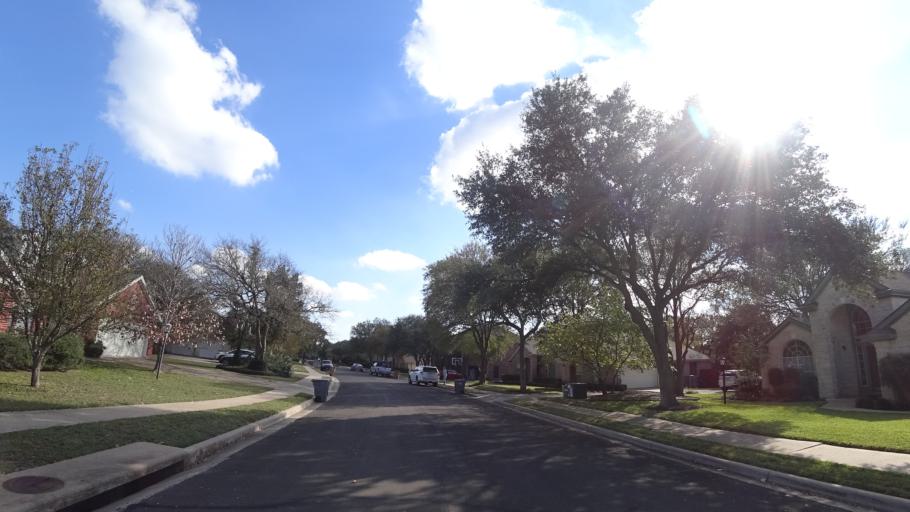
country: US
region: Texas
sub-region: Travis County
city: Shady Hollow
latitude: 30.1821
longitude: -97.8619
